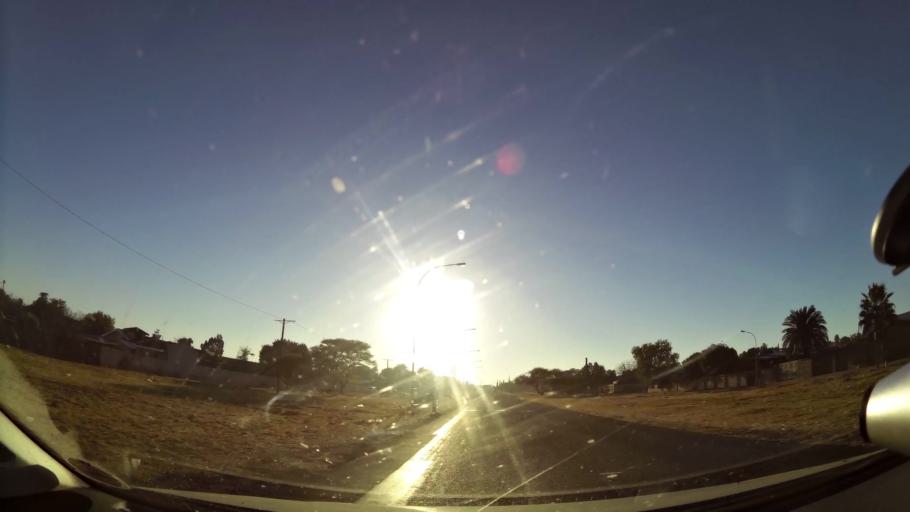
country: ZA
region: Northern Cape
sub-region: Frances Baard District Municipality
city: Kimberley
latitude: -28.7531
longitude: 24.7314
